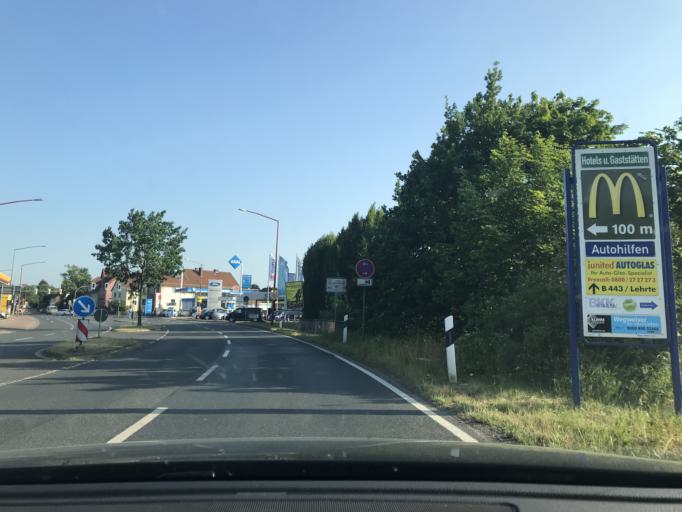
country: DE
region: Lower Saxony
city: Lehrte
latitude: 52.3881
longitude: 9.9703
